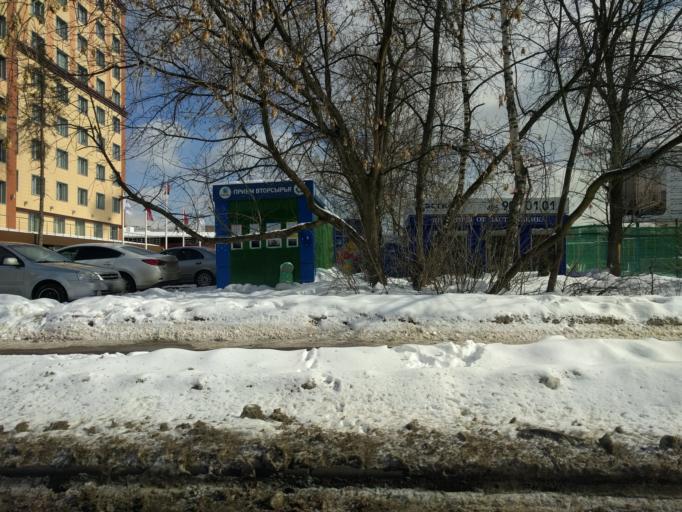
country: RU
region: Moscow
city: Metrogorodok
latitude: 55.8000
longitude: 37.7751
